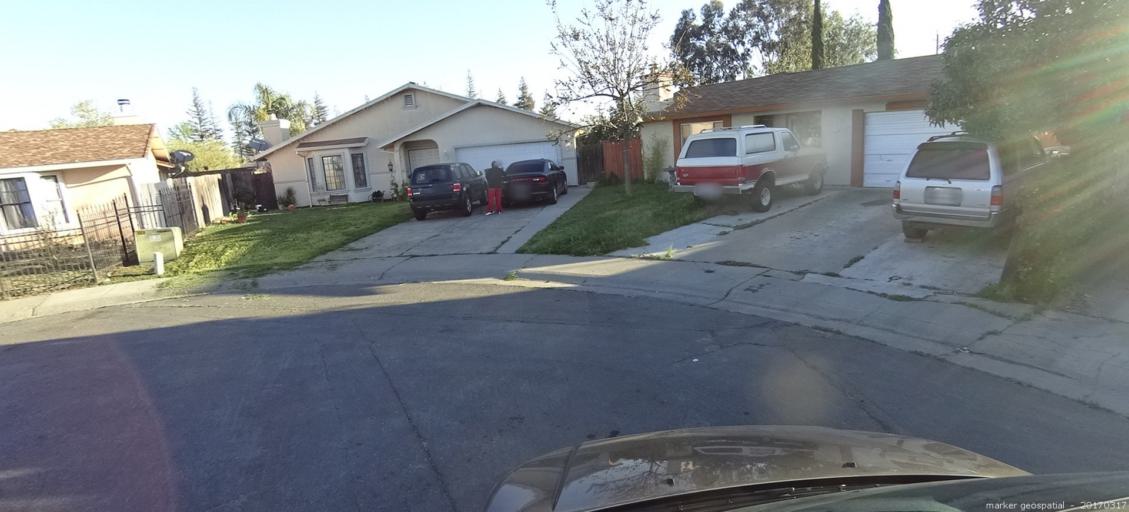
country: US
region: California
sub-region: Sacramento County
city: Parkway
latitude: 38.4886
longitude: -121.4813
